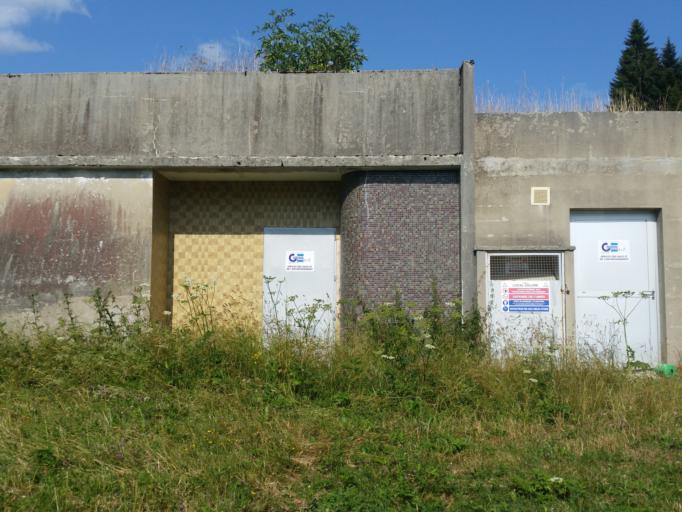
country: FR
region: Franche-Comte
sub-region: Departement du Doubs
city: Jougne
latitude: 46.7629
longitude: 6.3473
